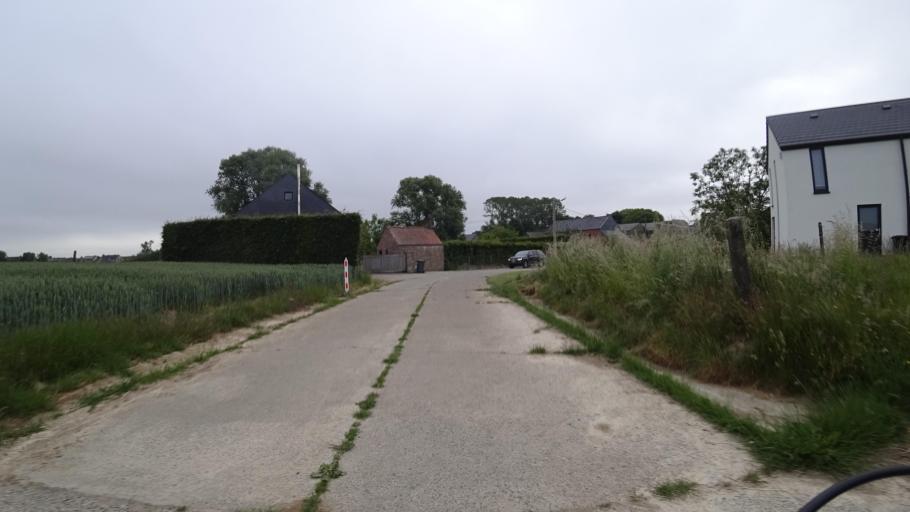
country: BE
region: Wallonia
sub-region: Province de Namur
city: Gembloux
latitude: 50.5340
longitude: 4.7770
